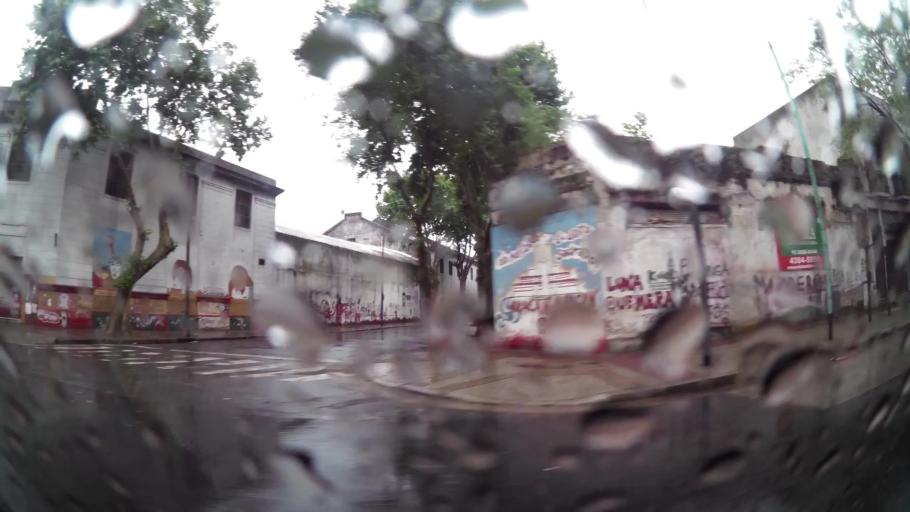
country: AR
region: Buenos Aires
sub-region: Partido de Avellaneda
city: Avellaneda
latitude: -34.6432
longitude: -58.3977
